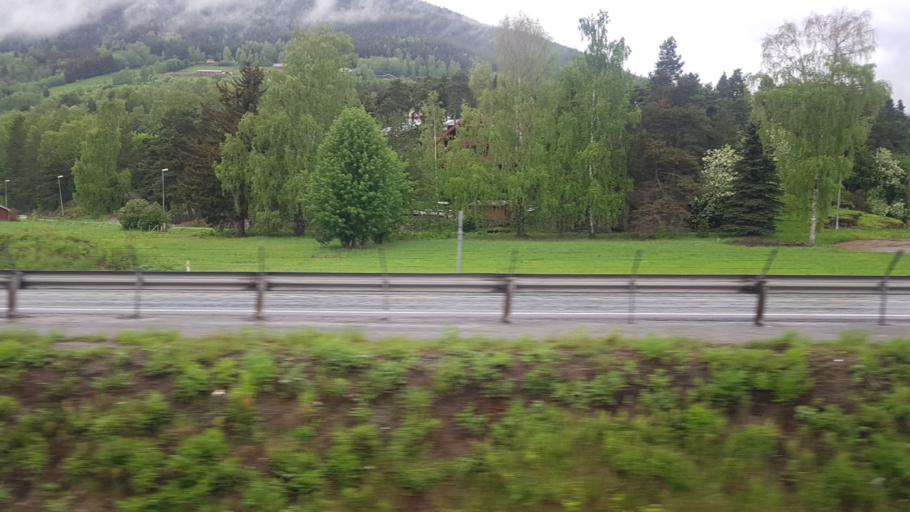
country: NO
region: Oppland
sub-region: Sor-Fron
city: Hundorp
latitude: 61.5421
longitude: 10.0110
